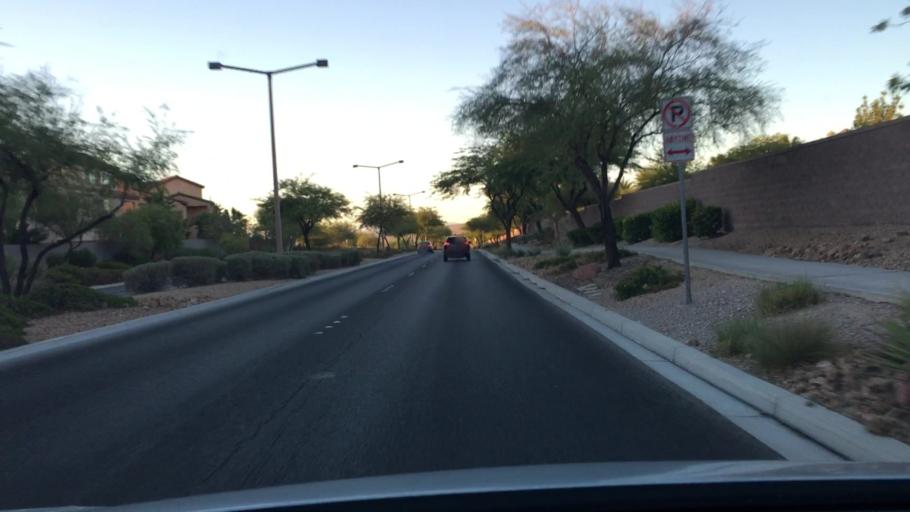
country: US
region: Nevada
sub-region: Clark County
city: Summerlin South
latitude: 36.1516
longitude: -115.3432
